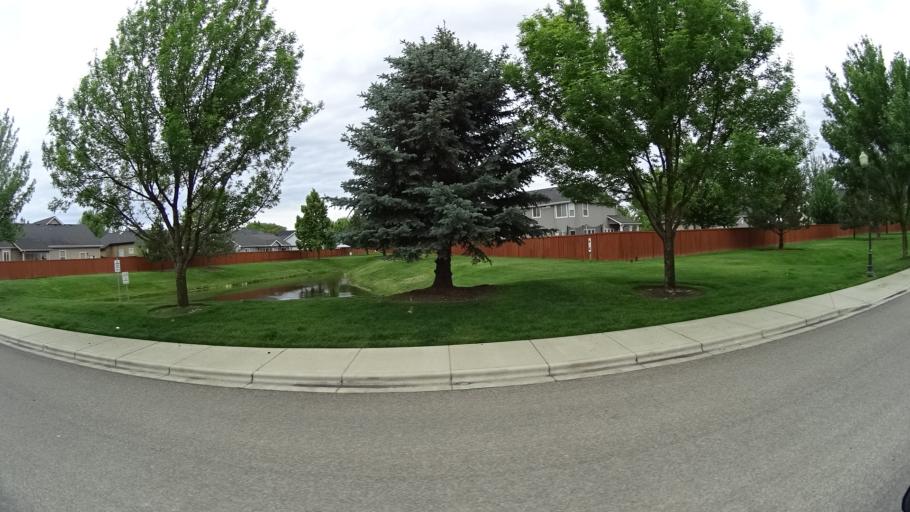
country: US
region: Idaho
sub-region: Ada County
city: Star
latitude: 43.6977
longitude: -116.4802
